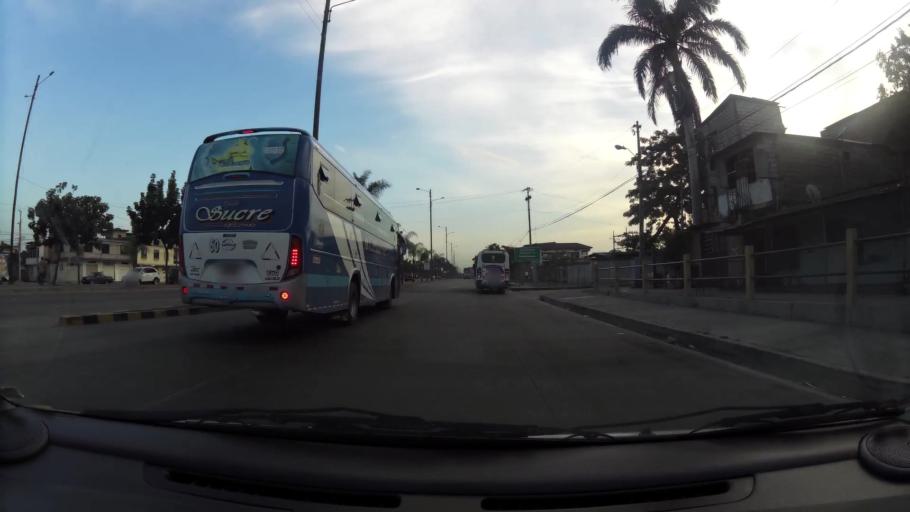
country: EC
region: Guayas
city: Eloy Alfaro
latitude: -2.1272
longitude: -79.8823
